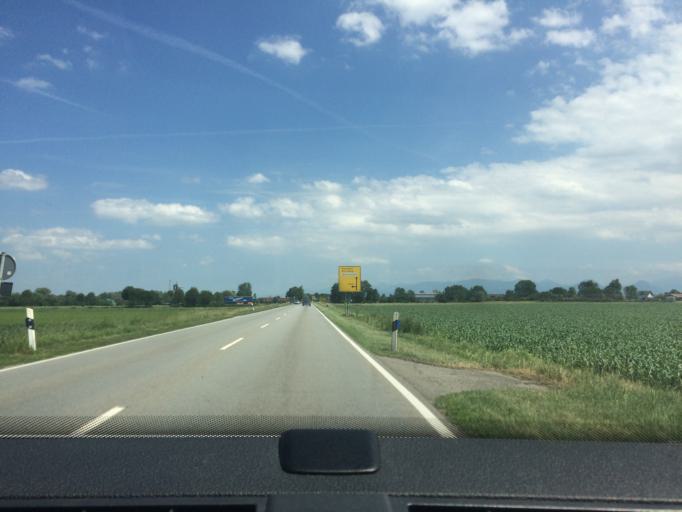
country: DE
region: Bavaria
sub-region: Upper Bavaria
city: Bruckmuhl
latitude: 47.8888
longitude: 11.9229
